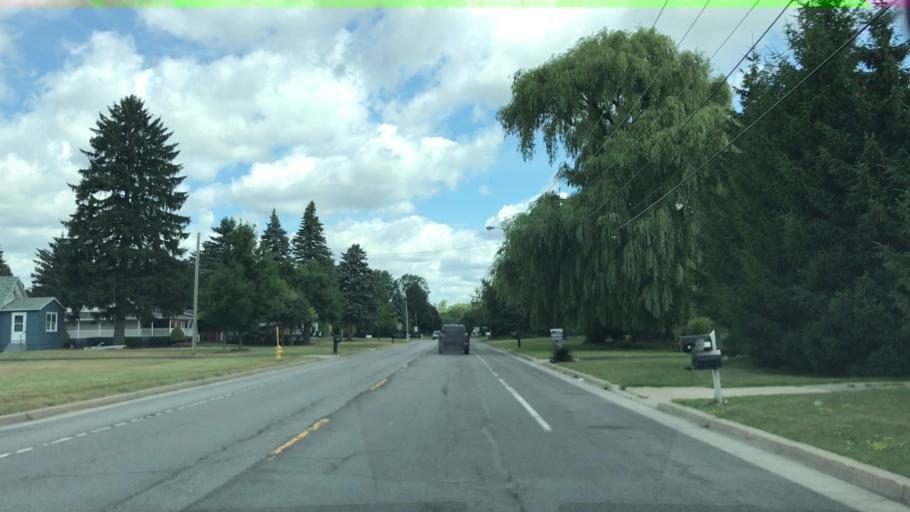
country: US
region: New York
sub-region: Erie County
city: Depew
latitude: 42.8942
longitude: -78.7086
